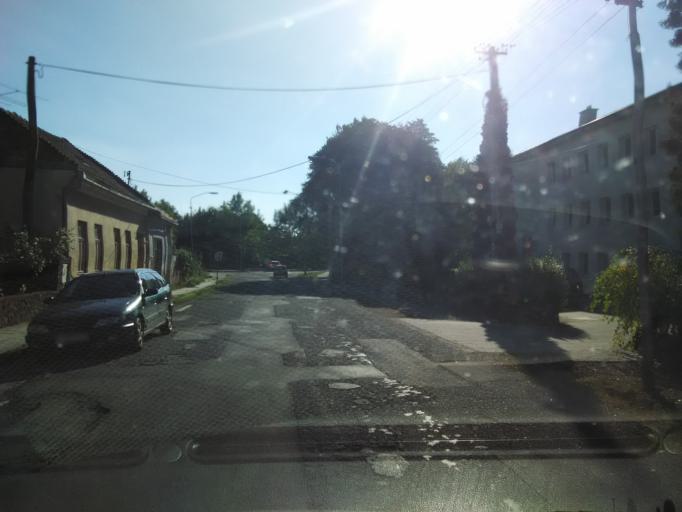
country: SK
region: Nitriansky
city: Levice
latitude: 48.2232
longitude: 18.6020
